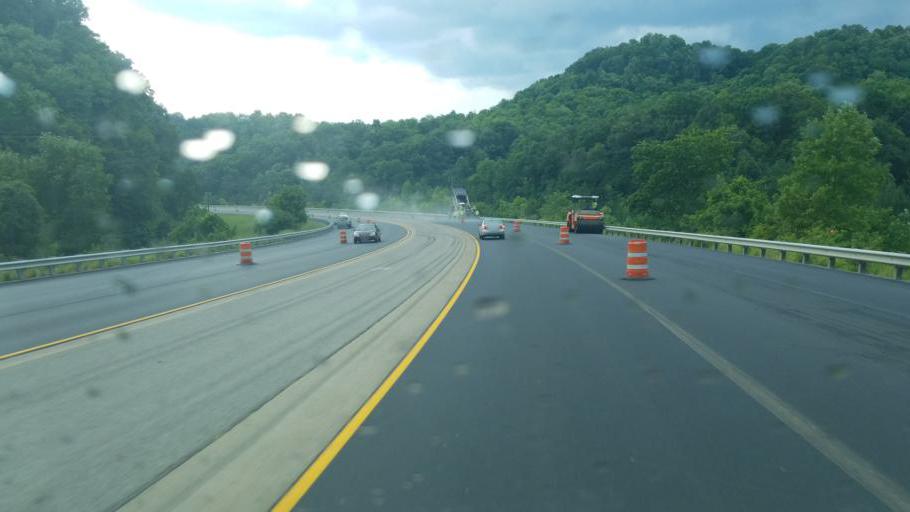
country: US
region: Kentucky
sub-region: Pike County
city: Pikeville
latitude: 37.5134
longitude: -82.5054
